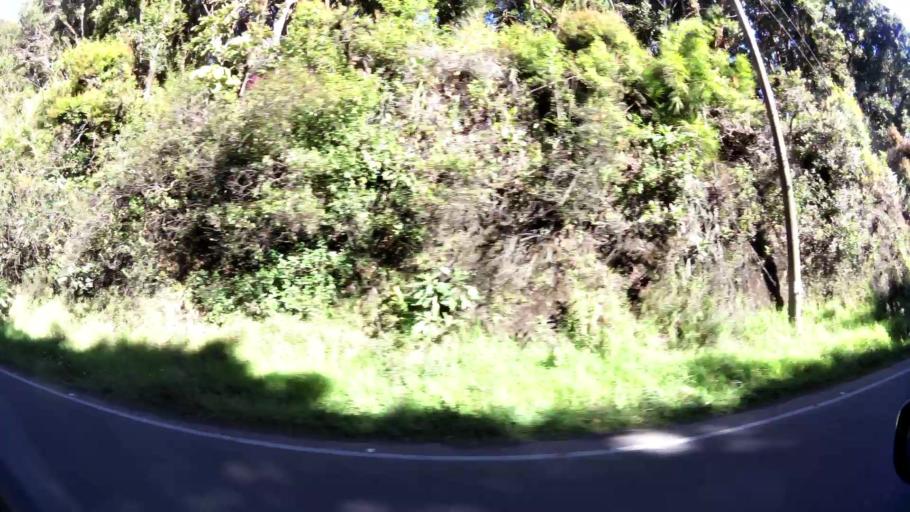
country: CR
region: San Jose
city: San Marcos
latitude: 9.6830
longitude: -83.9186
